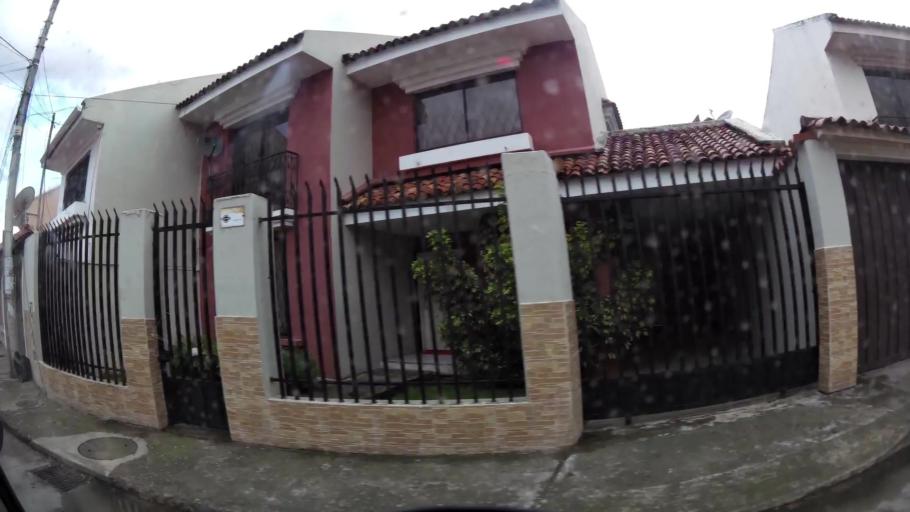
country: EC
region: Azuay
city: Cuenca
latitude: -2.9029
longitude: -79.0249
